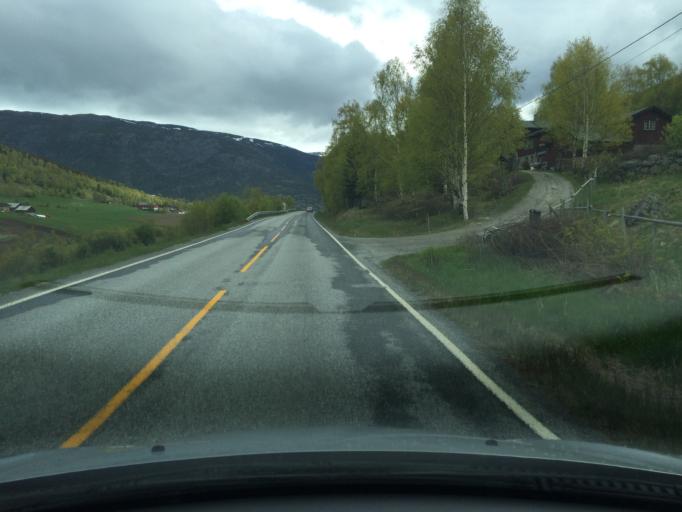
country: NO
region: Oppland
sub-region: Lom
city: Fossbergom
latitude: 61.8236
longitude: 8.5409
